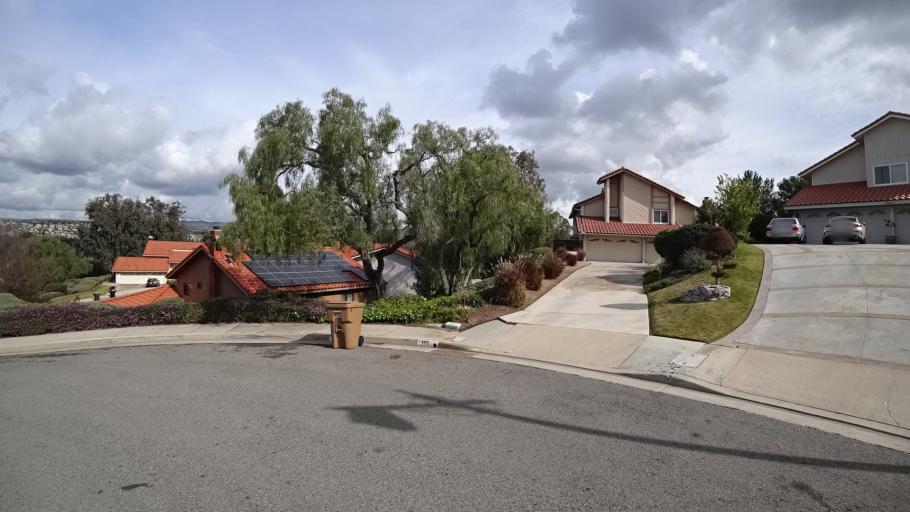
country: US
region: California
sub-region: Orange County
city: Yorba Linda
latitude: 33.8552
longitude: -117.7695
